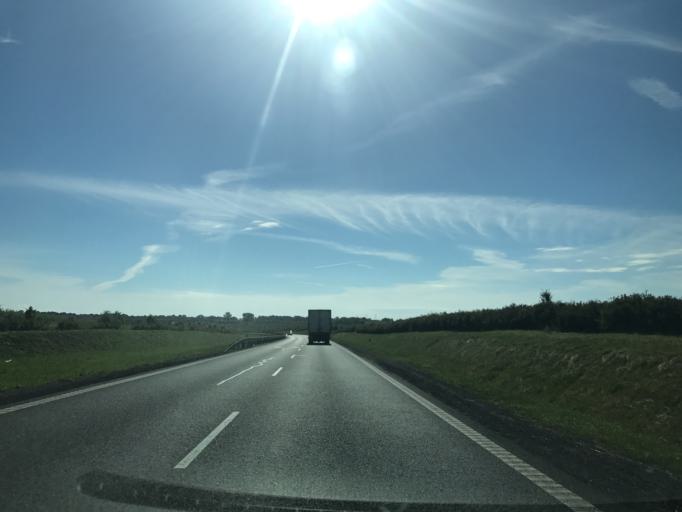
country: PL
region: Pomeranian Voivodeship
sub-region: Powiat chojnicki
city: Chojnice
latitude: 53.6807
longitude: 17.5487
